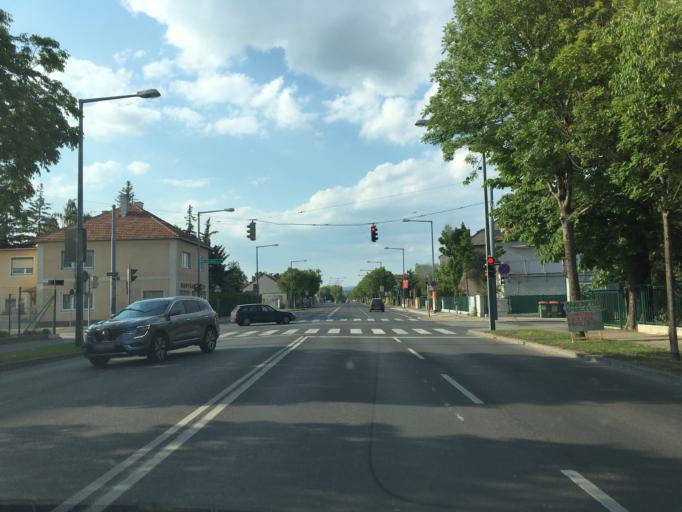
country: AT
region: Lower Austria
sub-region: Politischer Bezirk Modling
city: Vosendorf
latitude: 48.1409
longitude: 16.3239
